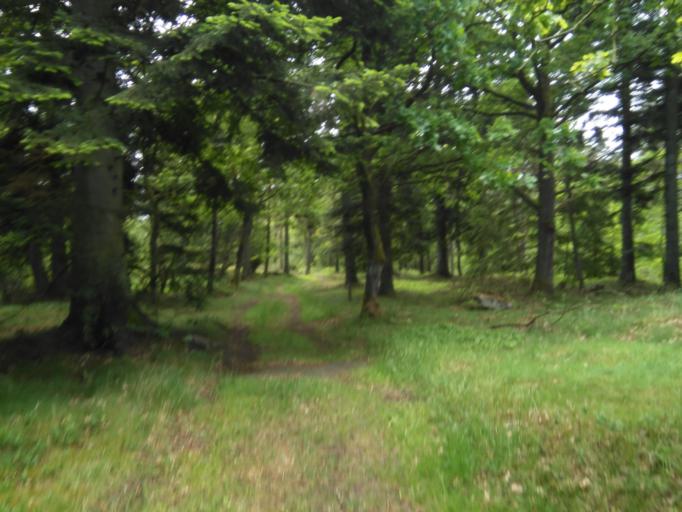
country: DK
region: Capital Region
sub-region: Bornholm Kommune
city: Nexo
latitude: 55.0943
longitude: 15.1035
